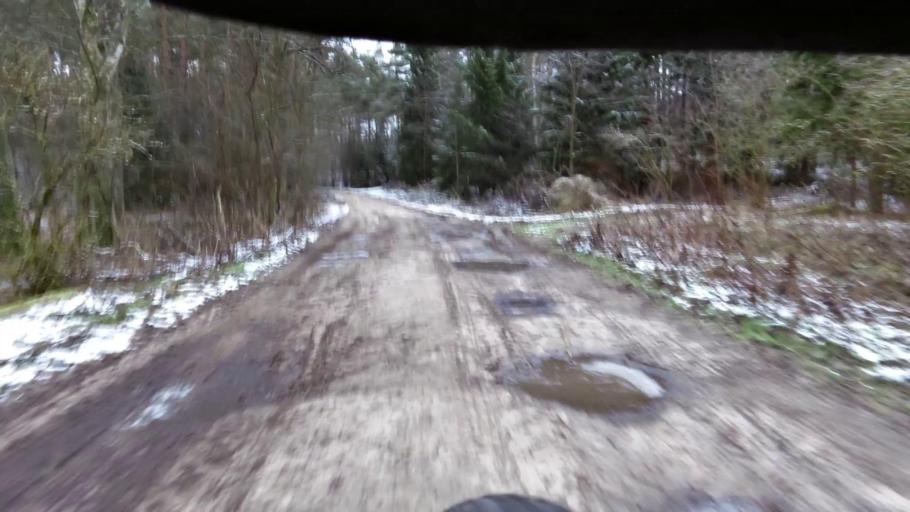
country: PL
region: West Pomeranian Voivodeship
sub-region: Powiat walecki
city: Miroslawiec
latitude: 53.2734
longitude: 16.0594
